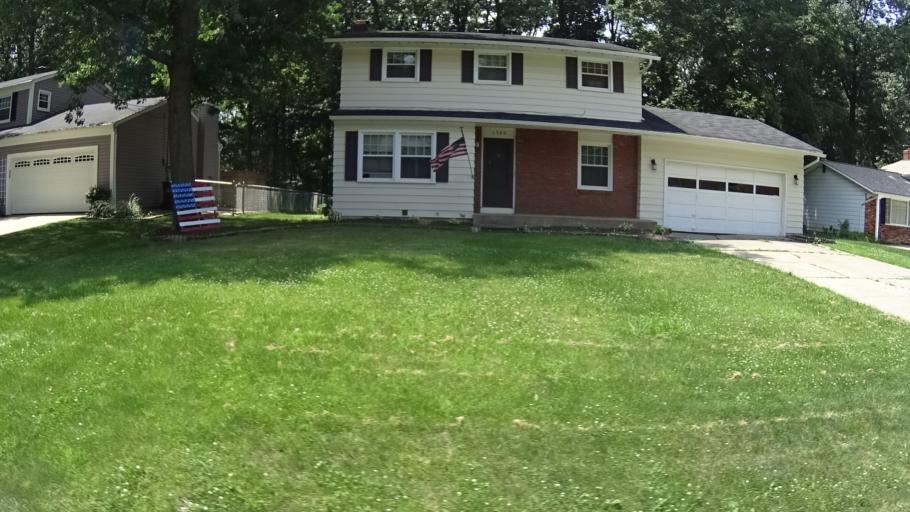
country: US
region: Ohio
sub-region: Lorain County
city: Vermilion
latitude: 41.4091
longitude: -82.3558
